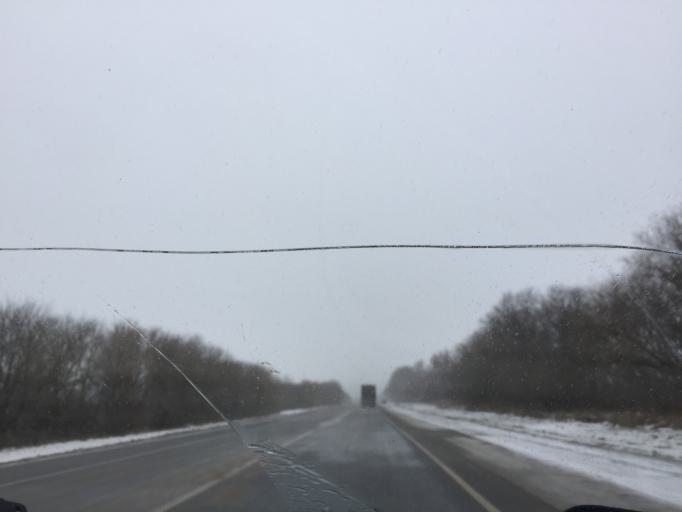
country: RU
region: Tula
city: Plavsk
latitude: 53.7835
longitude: 37.3617
